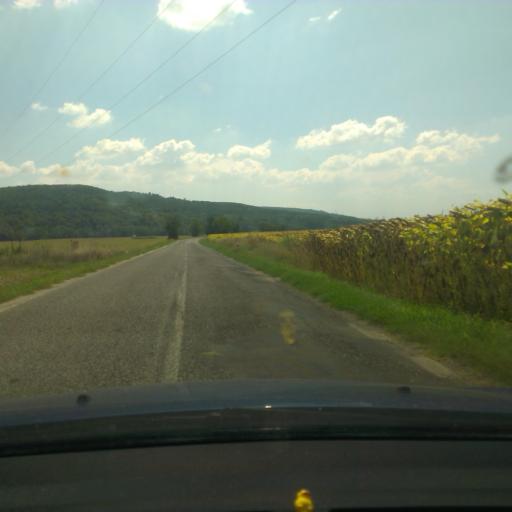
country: SK
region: Trnavsky
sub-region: Okres Trnava
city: Piestany
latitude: 48.5307
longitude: 17.8320
